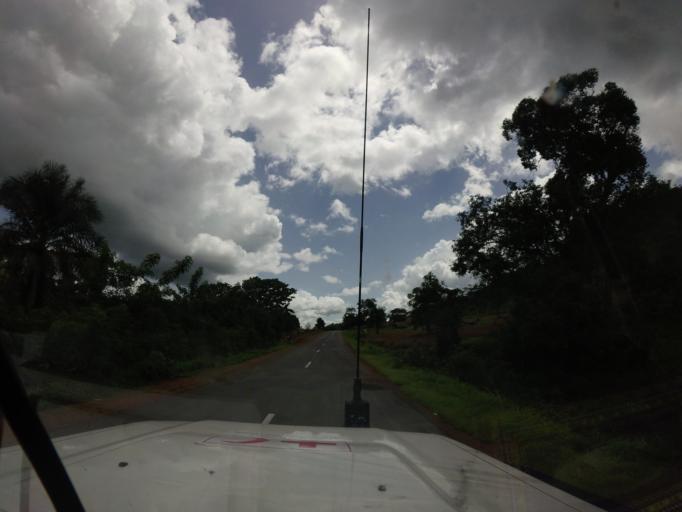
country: SL
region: Northern Province
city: Bindi
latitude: 10.1495
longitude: -11.5556
